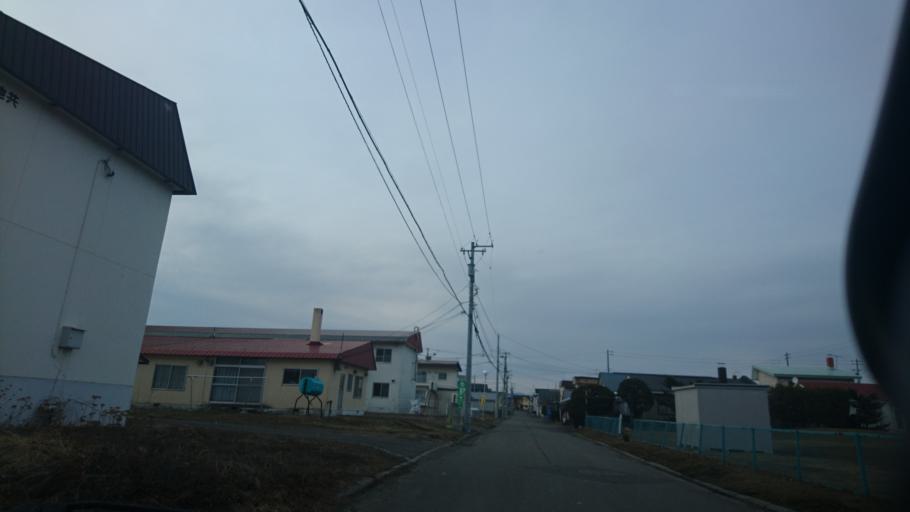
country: JP
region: Hokkaido
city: Otofuke
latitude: 42.9937
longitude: 143.1905
